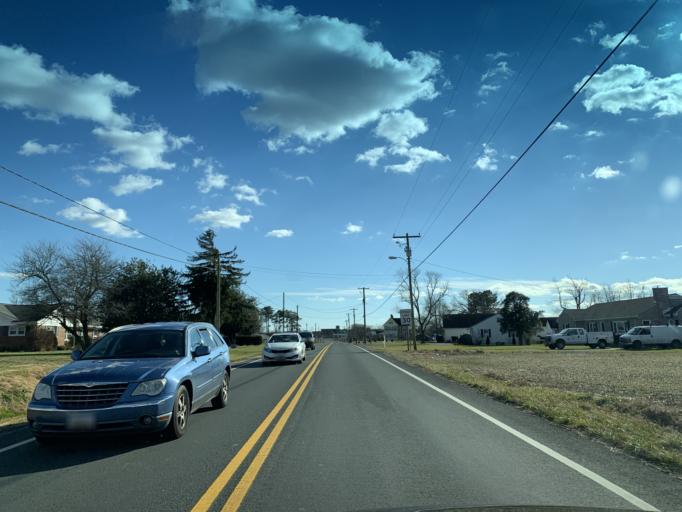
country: US
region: Maryland
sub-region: Worcester County
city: Berlin
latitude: 38.3479
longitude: -75.1922
